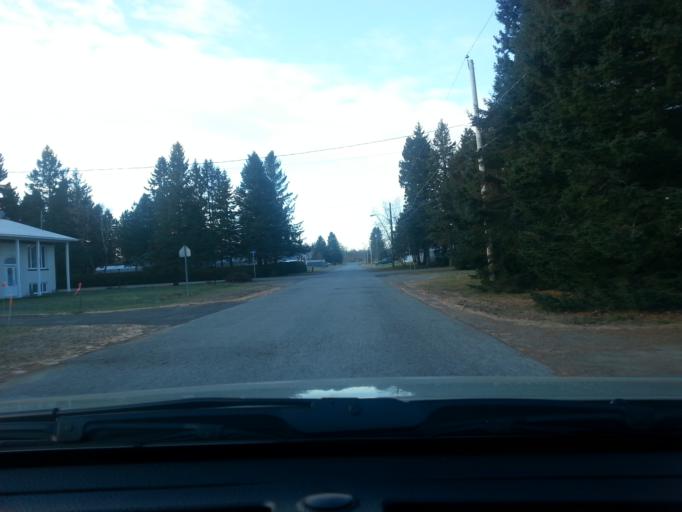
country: CA
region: Quebec
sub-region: Capitale-Nationale
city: Saint-Marc-des-Carrieres
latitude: 46.6832
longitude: -72.0697
